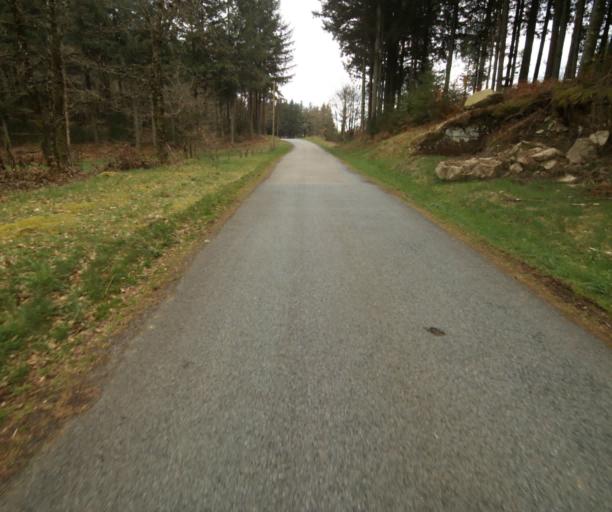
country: FR
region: Limousin
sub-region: Departement de la Correze
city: Correze
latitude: 45.3239
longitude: 1.9167
